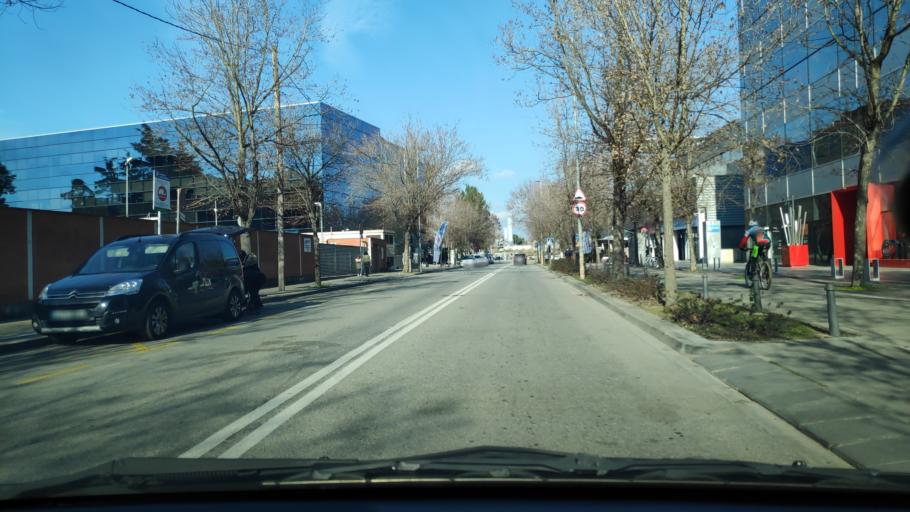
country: ES
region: Catalonia
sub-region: Provincia de Barcelona
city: Sant Cugat del Valles
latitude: 41.4742
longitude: 2.0974
